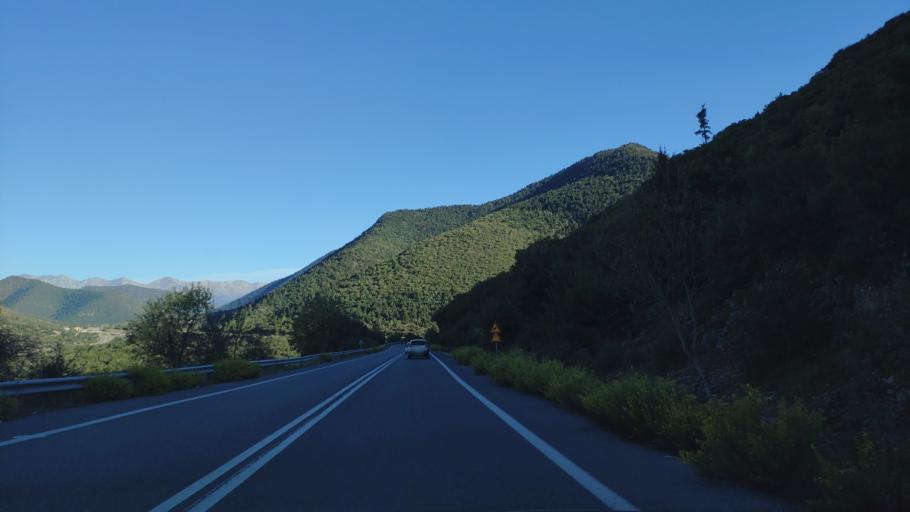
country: GR
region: Peloponnese
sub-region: Nomos Arkadias
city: Langadhia
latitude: 37.7270
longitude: 22.2092
